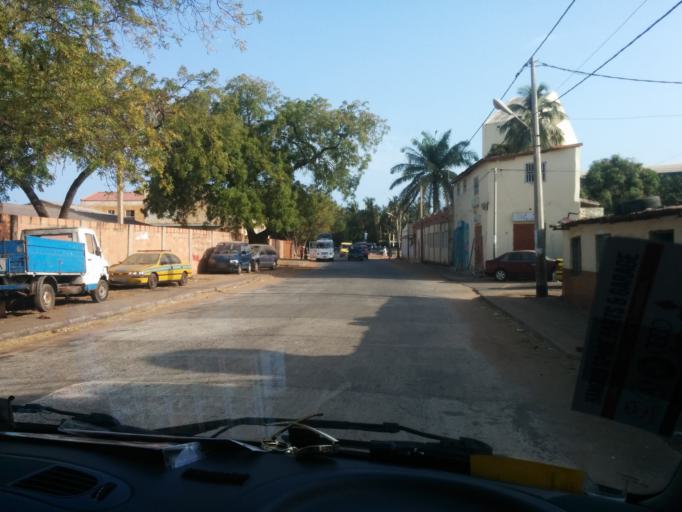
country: GM
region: Banjul
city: Banjul
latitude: 13.4591
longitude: -16.5829
